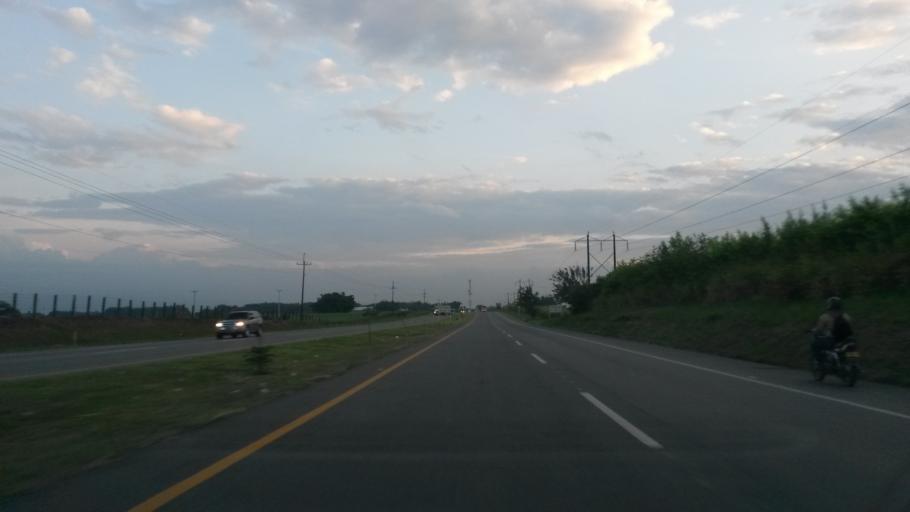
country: CO
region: Cauca
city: Santander de Quilichao
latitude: 3.0673
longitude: -76.4750
